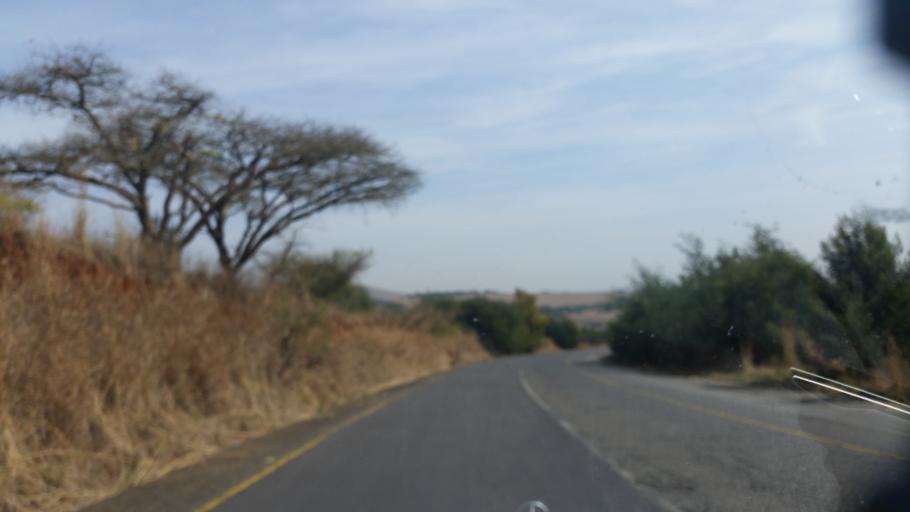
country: ZA
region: KwaZulu-Natal
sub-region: uMgungundlovu District Municipality
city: Mooirivier
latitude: -29.0945
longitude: 29.9677
